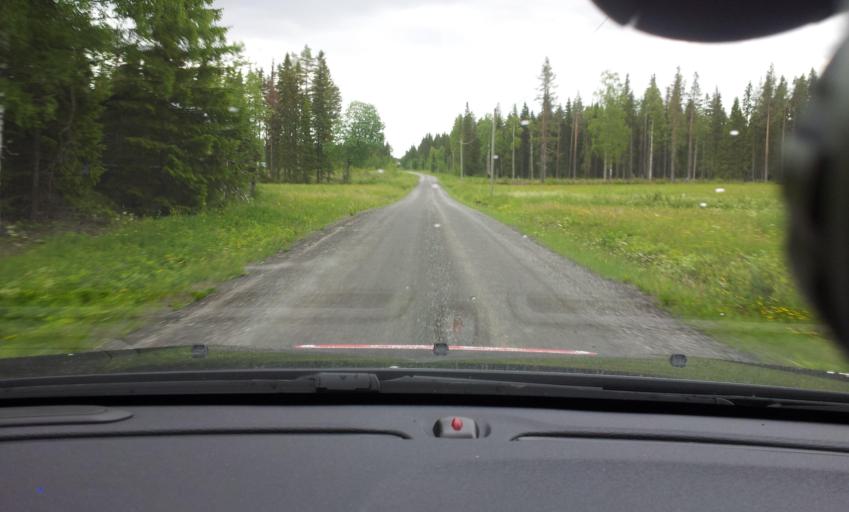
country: SE
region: Jaemtland
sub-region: OEstersunds Kommun
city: Brunflo
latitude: 63.1641
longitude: 15.0005
